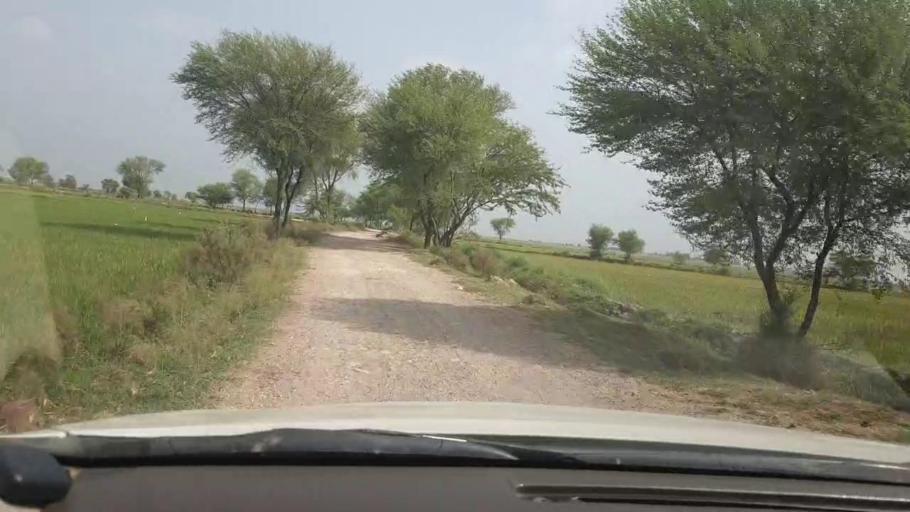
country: PK
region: Sindh
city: Shikarpur
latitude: 28.0186
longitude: 68.5936
